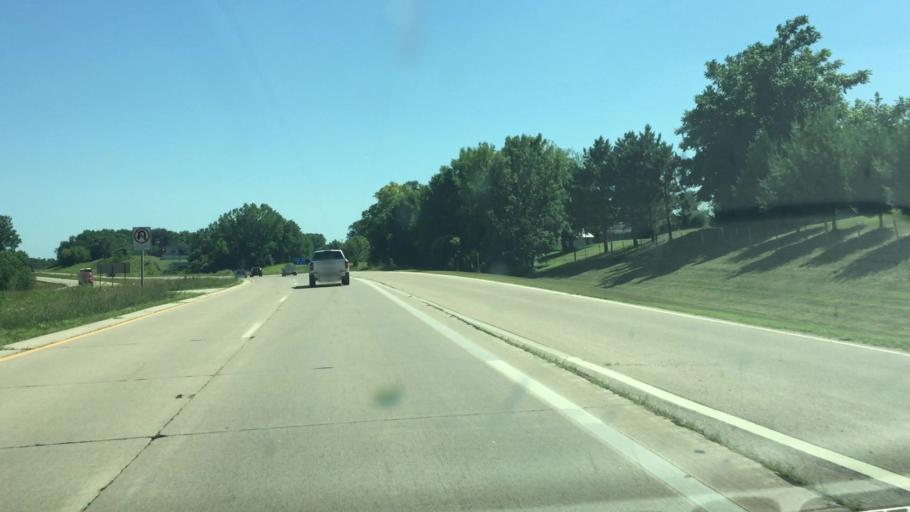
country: US
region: Illinois
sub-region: Jo Daviess County
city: East Dubuque
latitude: 42.5516
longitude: -90.6099
